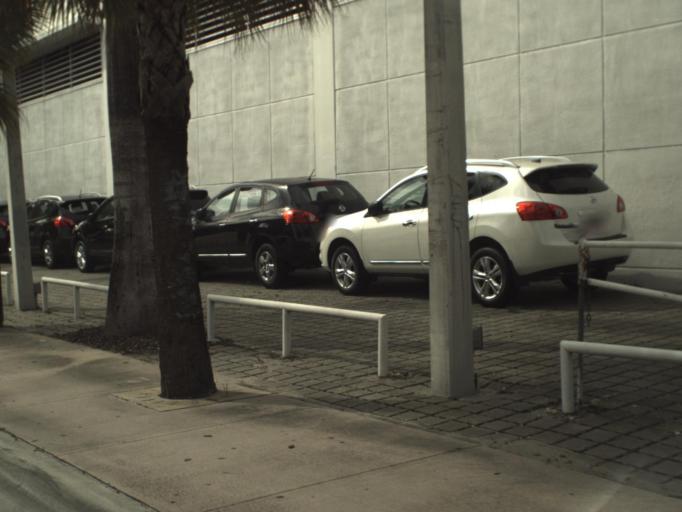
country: US
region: Florida
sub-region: Miami-Dade County
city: Coral Gables
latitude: 25.7650
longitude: -80.2483
